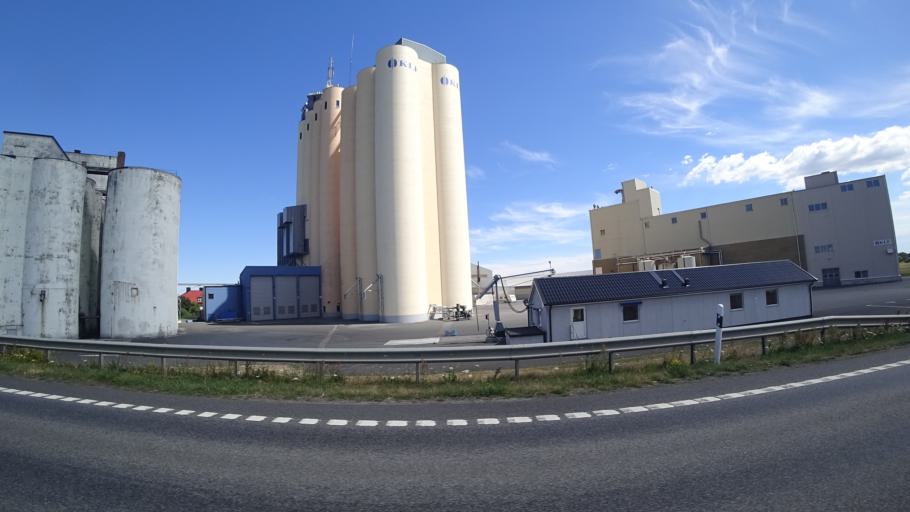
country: SE
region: Skane
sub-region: Kristianstads Kommun
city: Kristianstad
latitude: 56.0395
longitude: 14.0930
